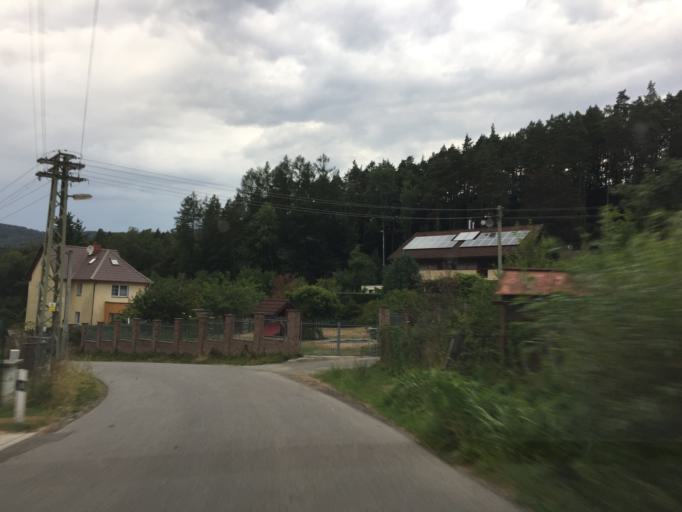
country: CZ
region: Liberecky
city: Mala Skala
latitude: 50.6395
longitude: 15.1995
